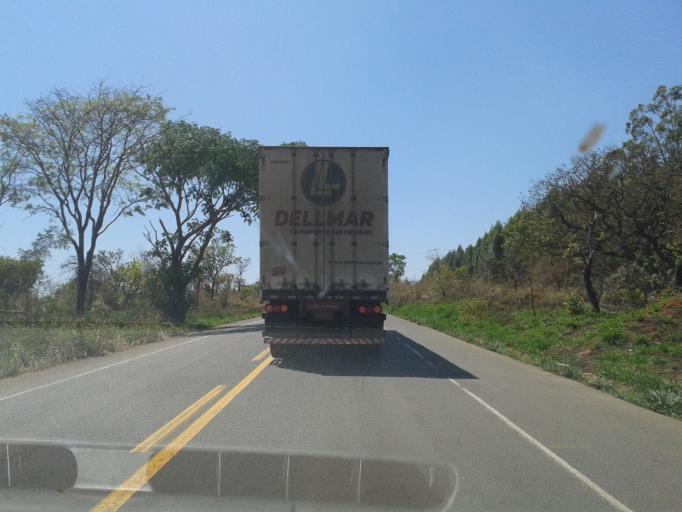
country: BR
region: Minas Gerais
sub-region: Araxa
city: Araxa
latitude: -19.4353
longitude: -47.2053
